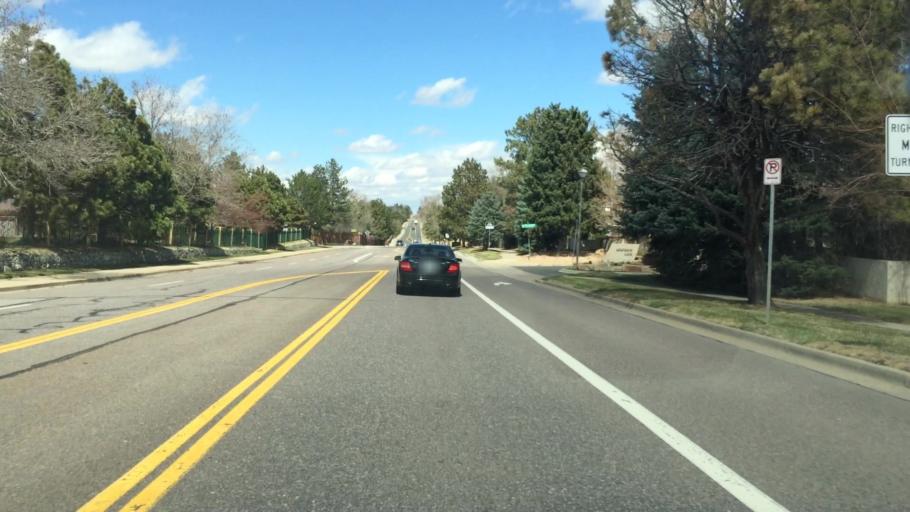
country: US
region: Colorado
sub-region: Arapahoe County
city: Centennial
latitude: 39.6045
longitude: -104.8761
